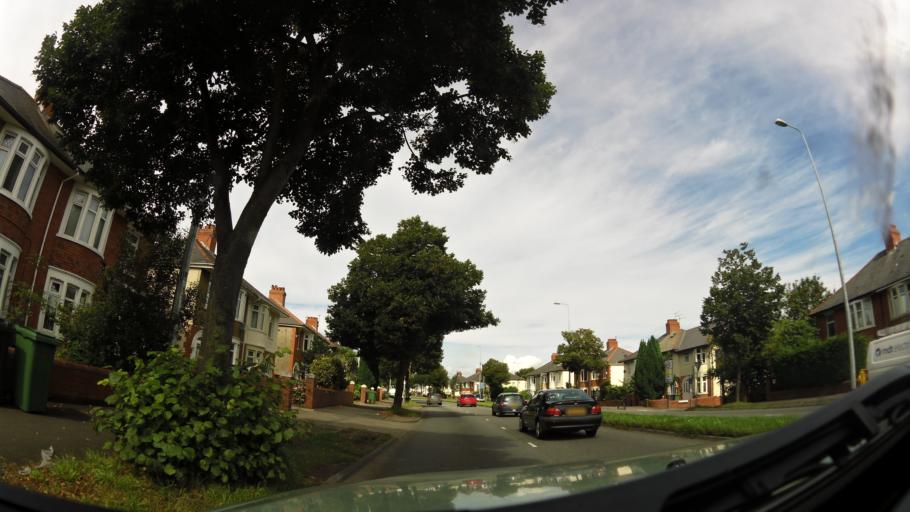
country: GB
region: Wales
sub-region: Cardiff
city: Cardiff
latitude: 51.5106
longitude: -3.2045
